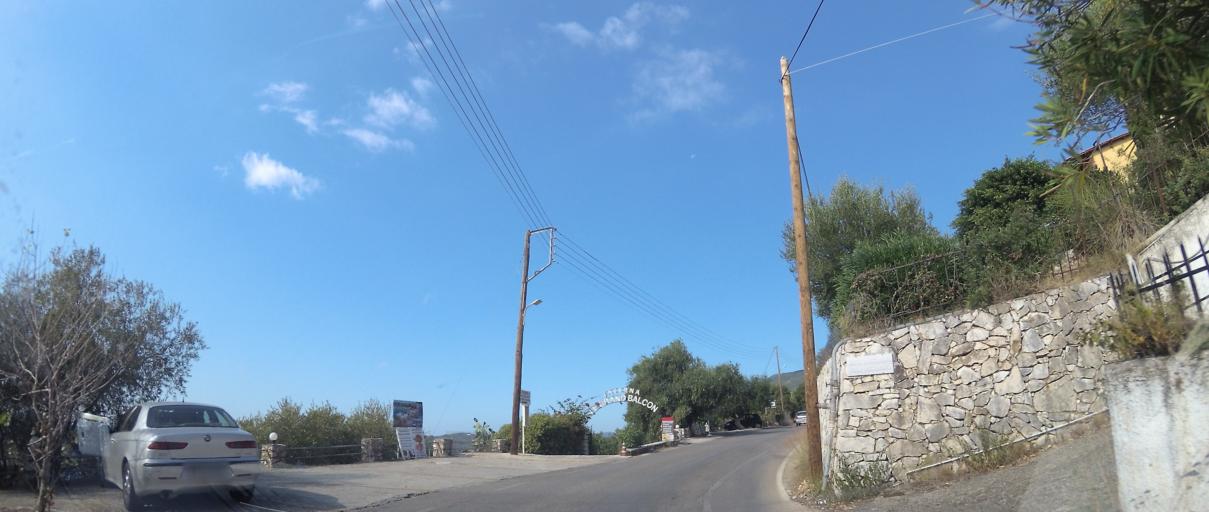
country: GR
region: Ionian Islands
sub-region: Nomos Kerkyras
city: Kontokali
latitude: 39.7085
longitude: 19.8485
